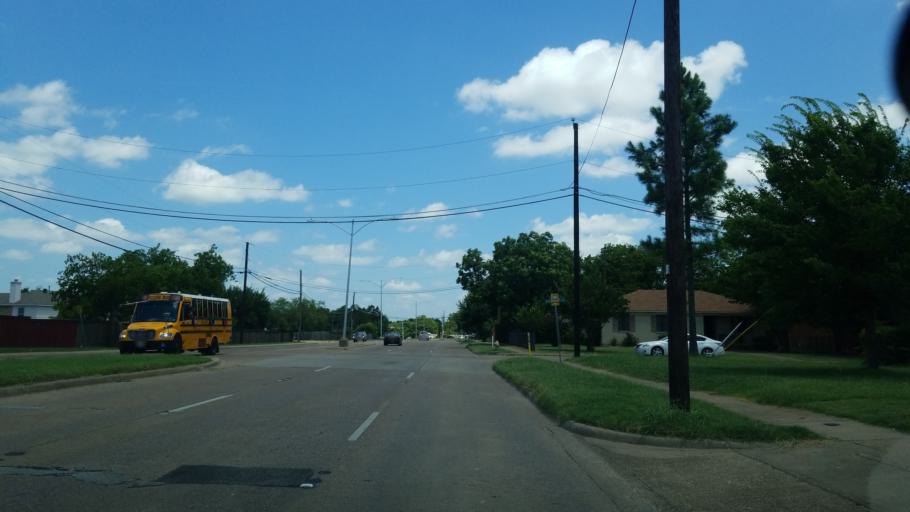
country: US
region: Texas
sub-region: Dallas County
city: Balch Springs
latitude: 32.7460
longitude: -96.7000
